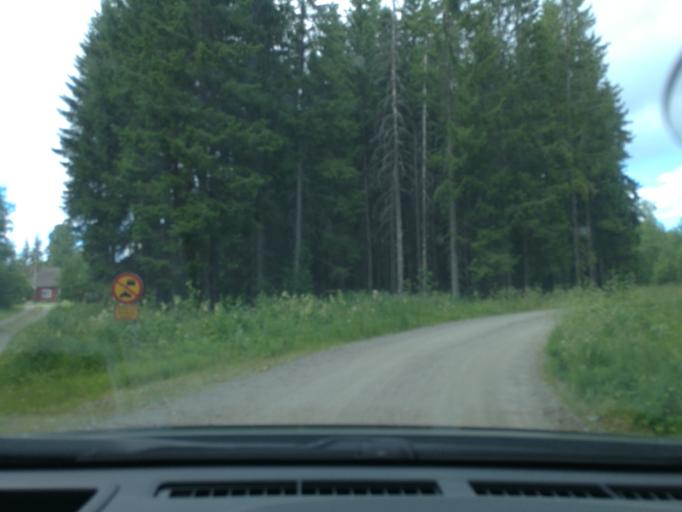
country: SE
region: Vaestmanland
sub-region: Surahammars Kommun
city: Ramnas
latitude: 59.8213
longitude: 16.2580
